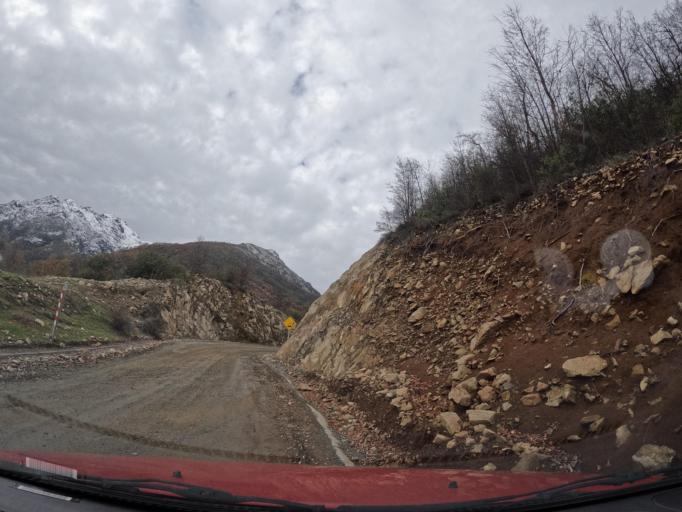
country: CL
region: Maule
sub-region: Provincia de Linares
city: Colbun
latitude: -35.8573
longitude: -71.1884
